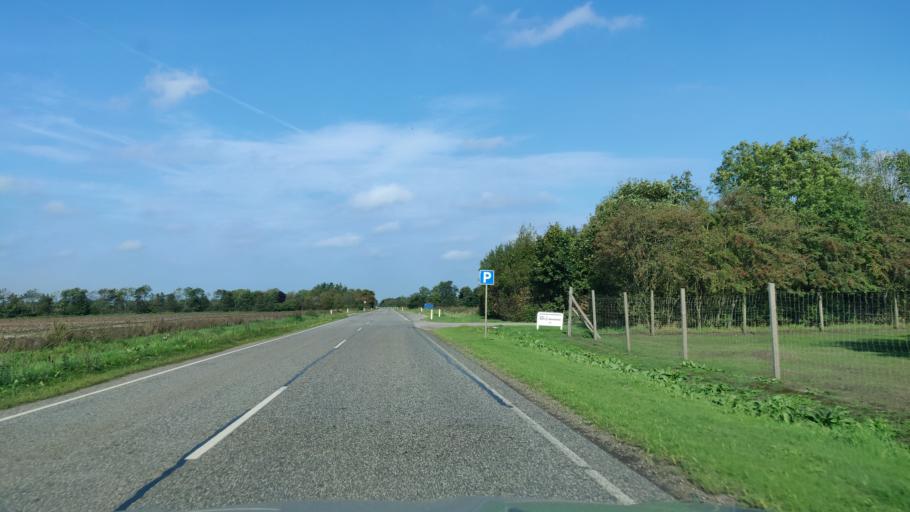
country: DK
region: Central Jutland
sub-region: Herning Kommune
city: Sunds
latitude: 56.2529
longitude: 9.0519
